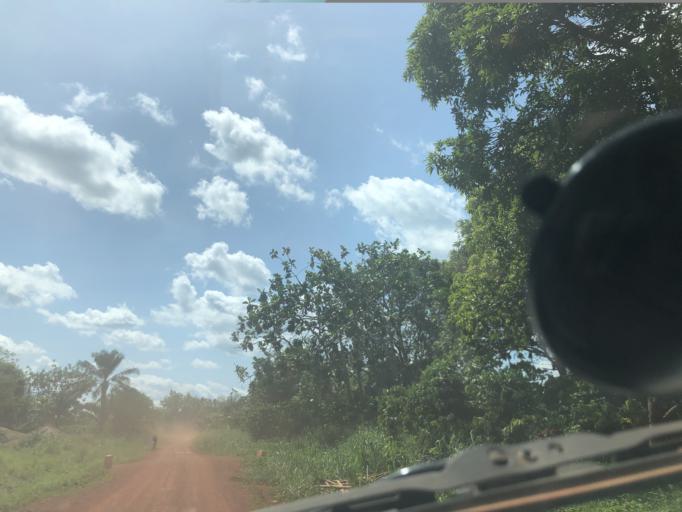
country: CD
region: Equateur
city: Libenge
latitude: 3.8403
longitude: 18.6830
